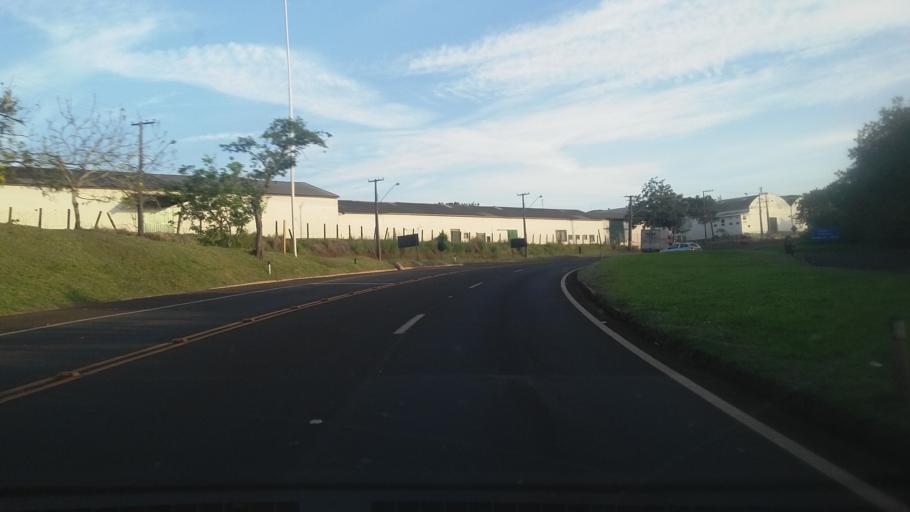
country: BR
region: Parana
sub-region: Assai
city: Assai
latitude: -23.1976
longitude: -50.6544
